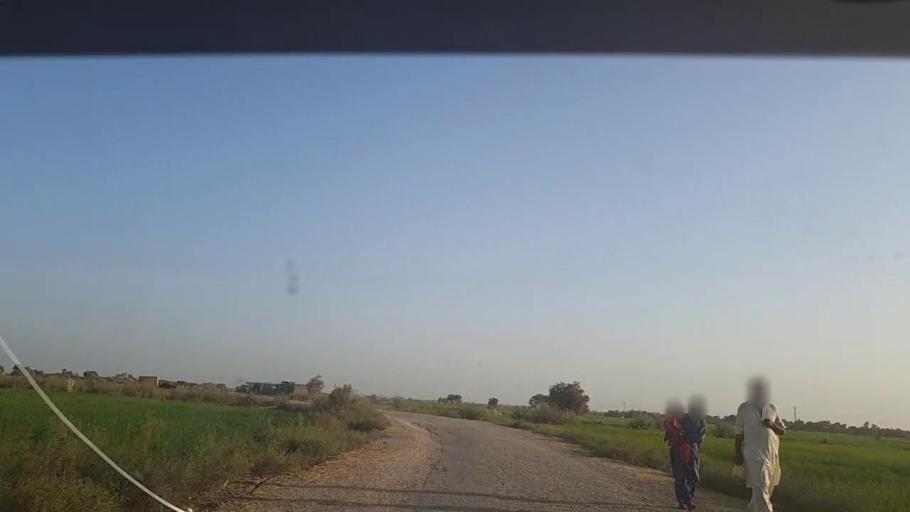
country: PK
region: Sindh
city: Thul
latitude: 28.1513
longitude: 68.8864
